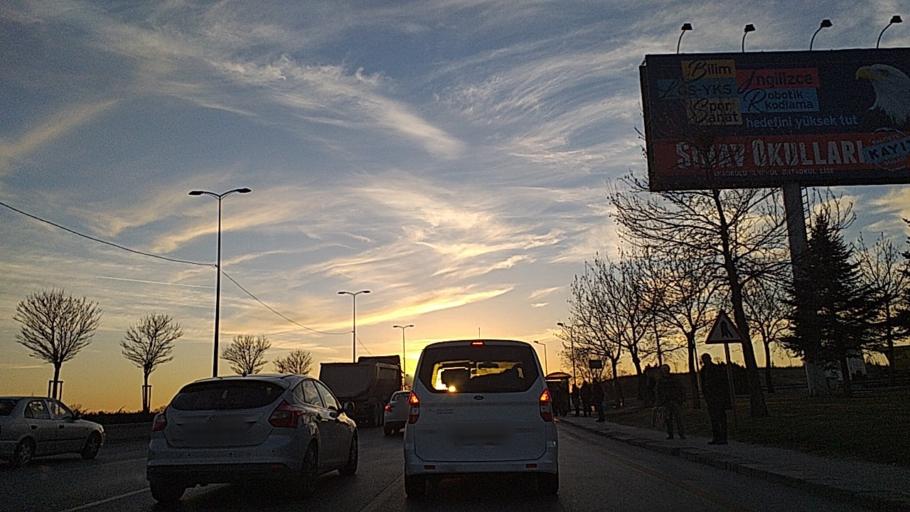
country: TR
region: Ankara
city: Etimesgut
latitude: 39.9634
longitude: 32.6758
